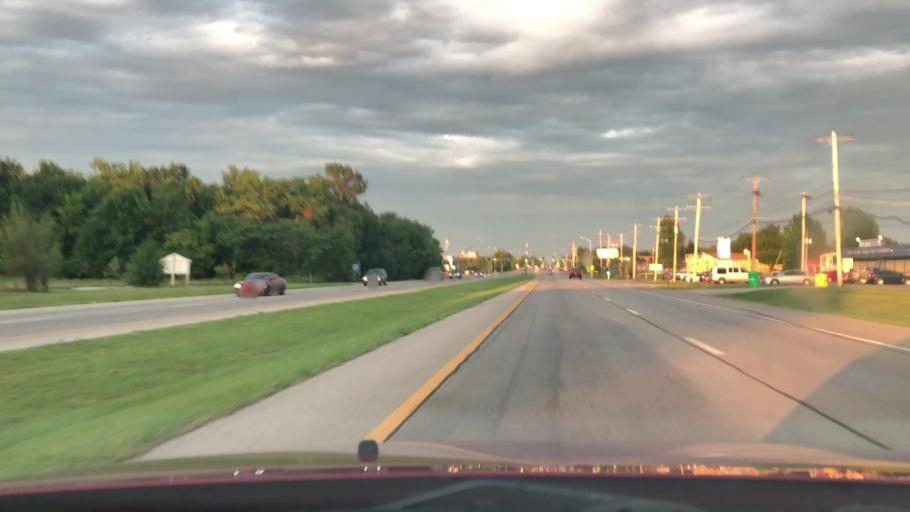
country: US
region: Missouri
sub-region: Greene County
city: Springfield
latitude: 37.1827
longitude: -93.3349
